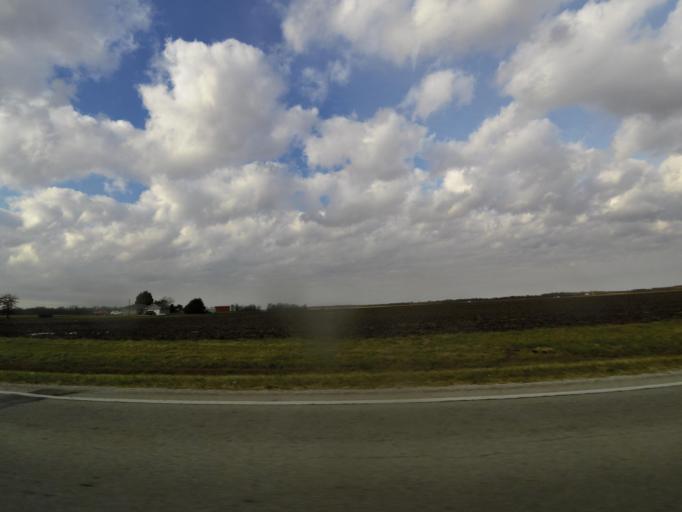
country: US
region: Illinois
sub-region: Fayette County
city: Ramsey
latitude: 39.2325
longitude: -89.1007
